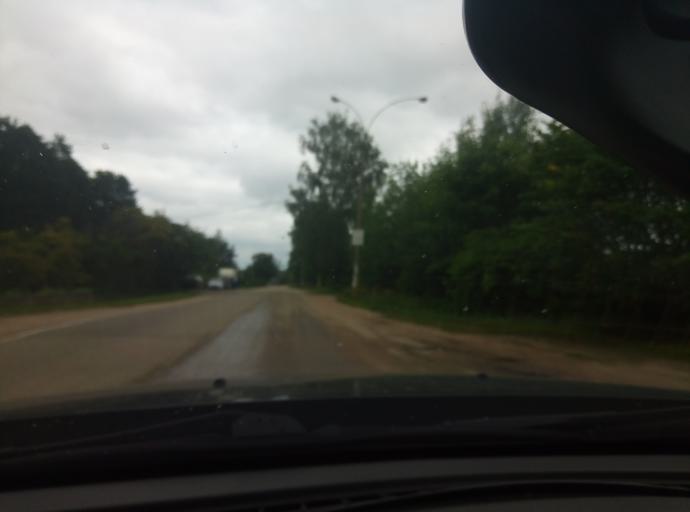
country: RU
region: Kaluga
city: Zhukovo
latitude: 54.9578
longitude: 36.7875
